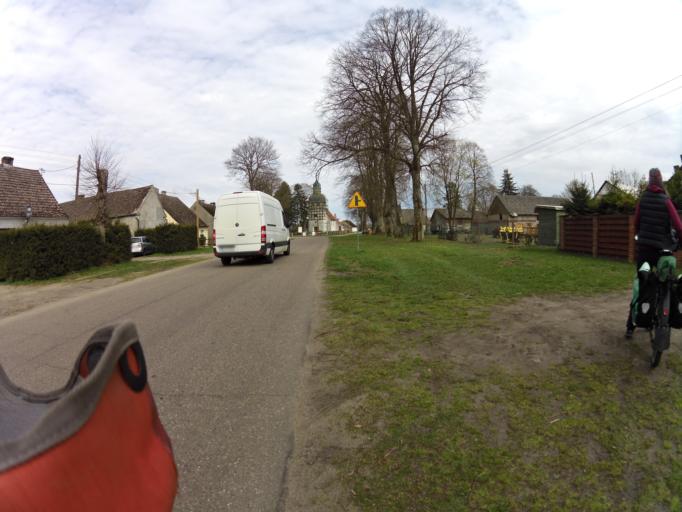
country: PL
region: West Pomeranian Voivodeship
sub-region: Powiat szczecinecki
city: Szczecinek
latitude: 53.8450
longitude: 16.6789
